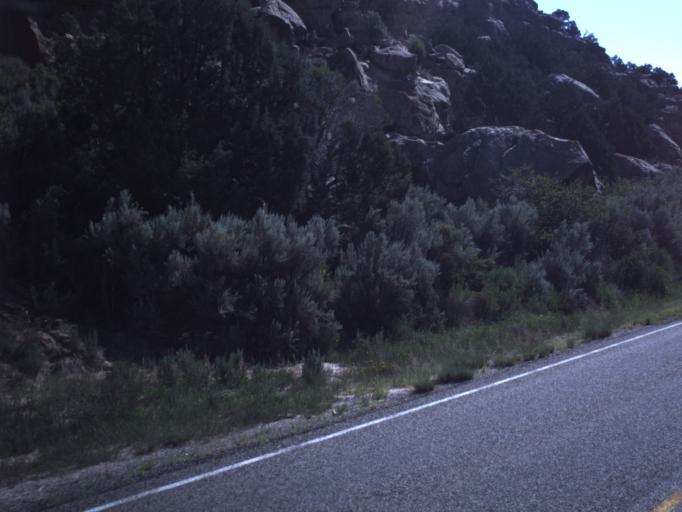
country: US
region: Utah
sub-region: Duchesne County
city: Duchesne
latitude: 40.3076
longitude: -110.6337
